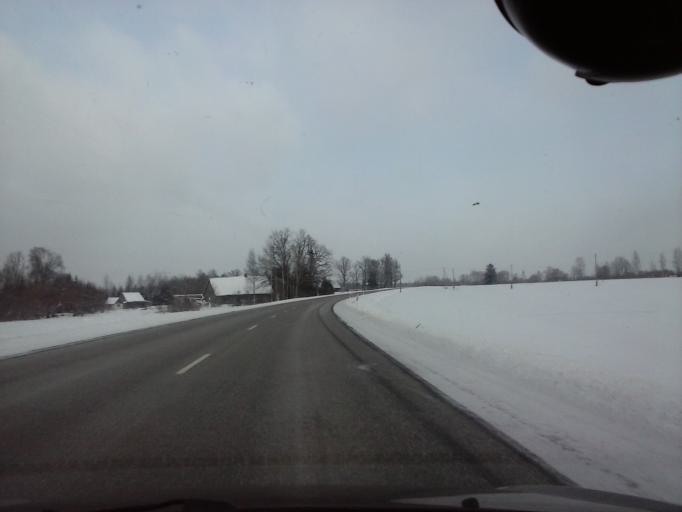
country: EE
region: Paernumaa
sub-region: Saarde vald
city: Kilingi-Nomme
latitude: 58.1747
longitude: 25.0356
